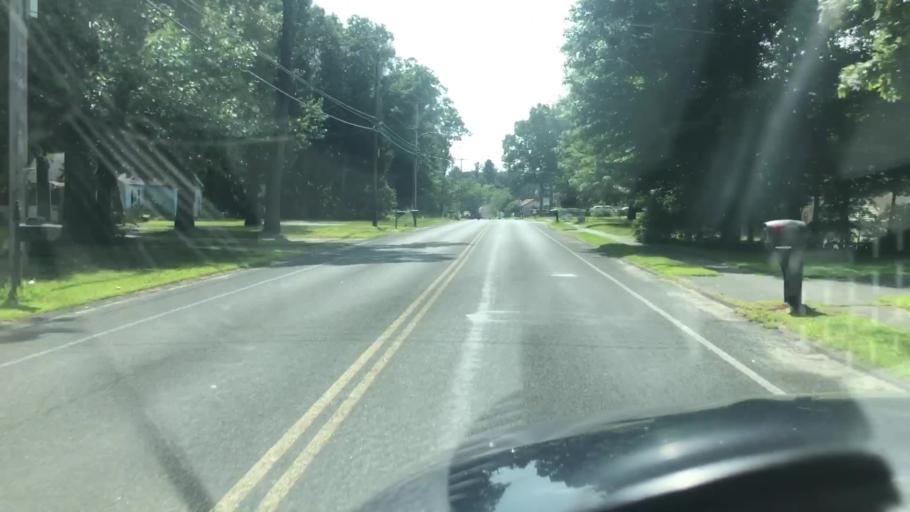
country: US
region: Massachusetts
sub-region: Hampshire County
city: Southampton
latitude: 42.1875
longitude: -72.6865
